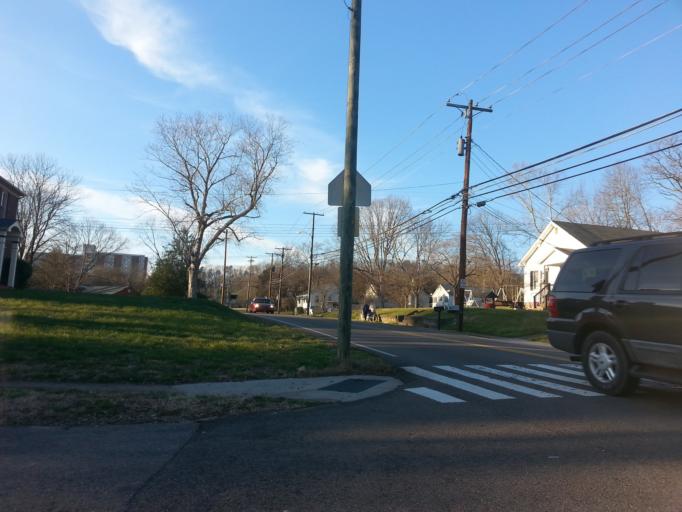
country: US
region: Tennessee
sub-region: Knox County
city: Knoxville
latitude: 36.0116
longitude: -83.9163
